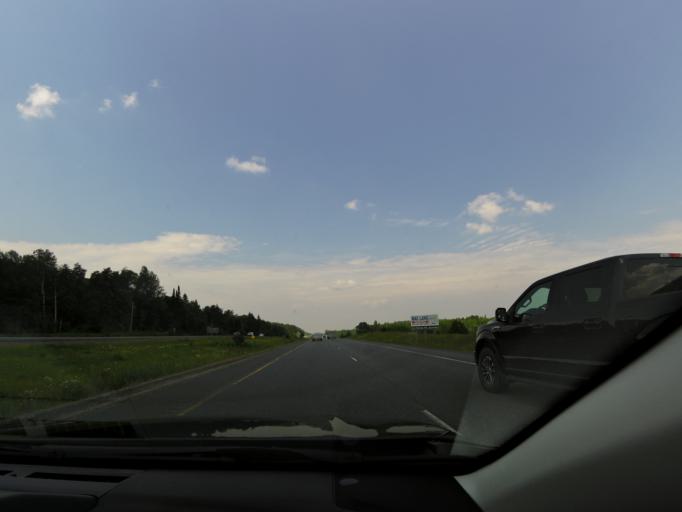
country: CA
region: Ontario
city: Huntsville
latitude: 45.4591
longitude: -79.2560
